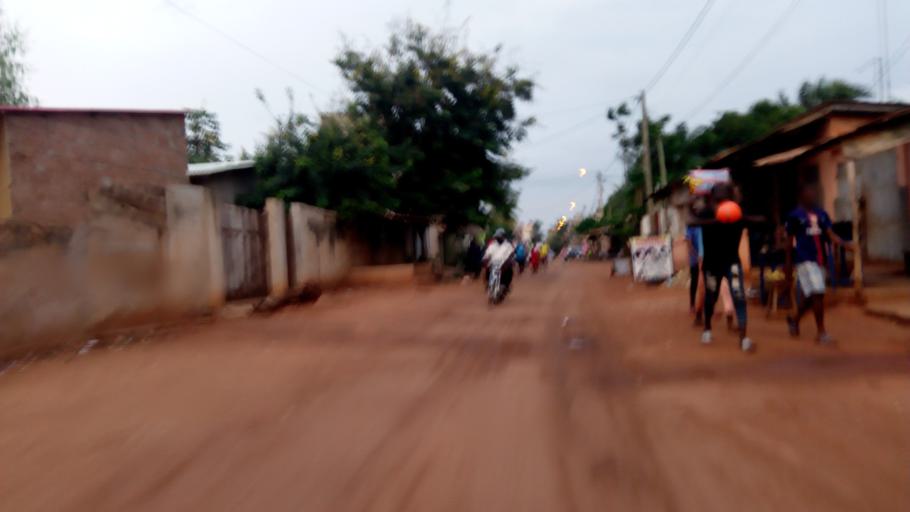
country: TG
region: Maritime
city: Lome
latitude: 6.2153
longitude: 1.2046
